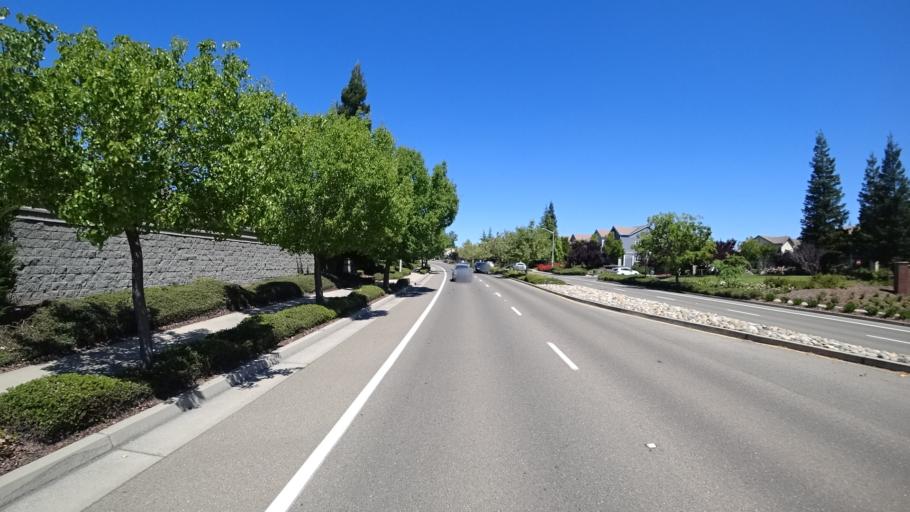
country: US
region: California
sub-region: Placer County
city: Roseville
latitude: 38.7971
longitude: -121.2881
